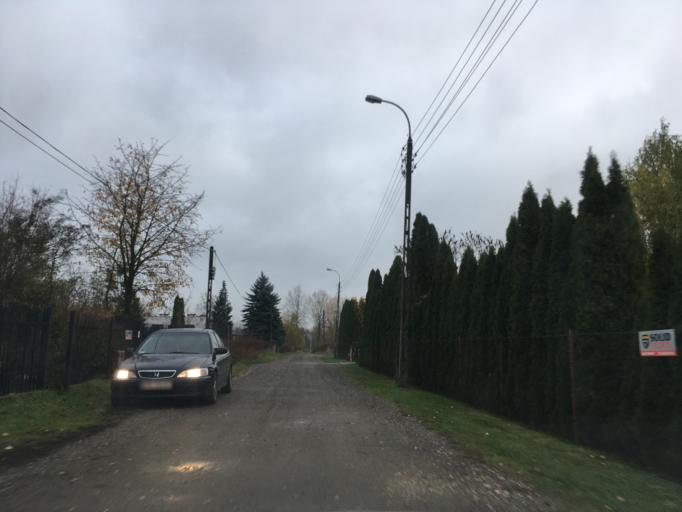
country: PL
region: Masovian Voivodeship
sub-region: Powiat pruszkowski
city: Brwinow
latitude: 52.1424
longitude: 20.7353
